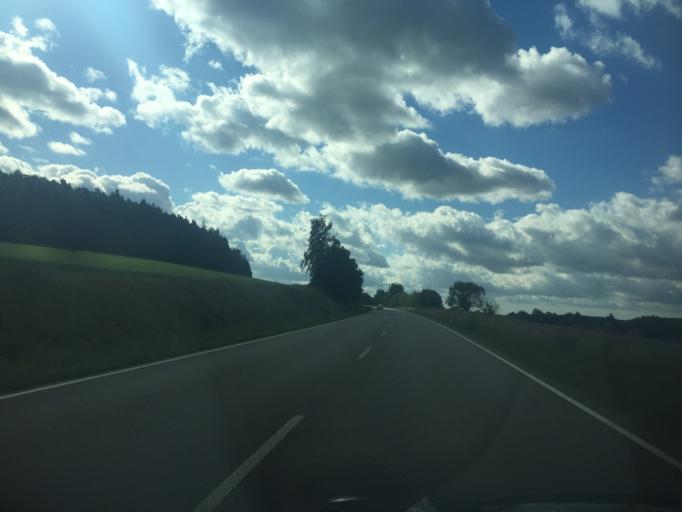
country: DE
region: Bavaria
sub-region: Upper Palatinate
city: Poppenricht
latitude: 49.5011
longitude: 11.8220
